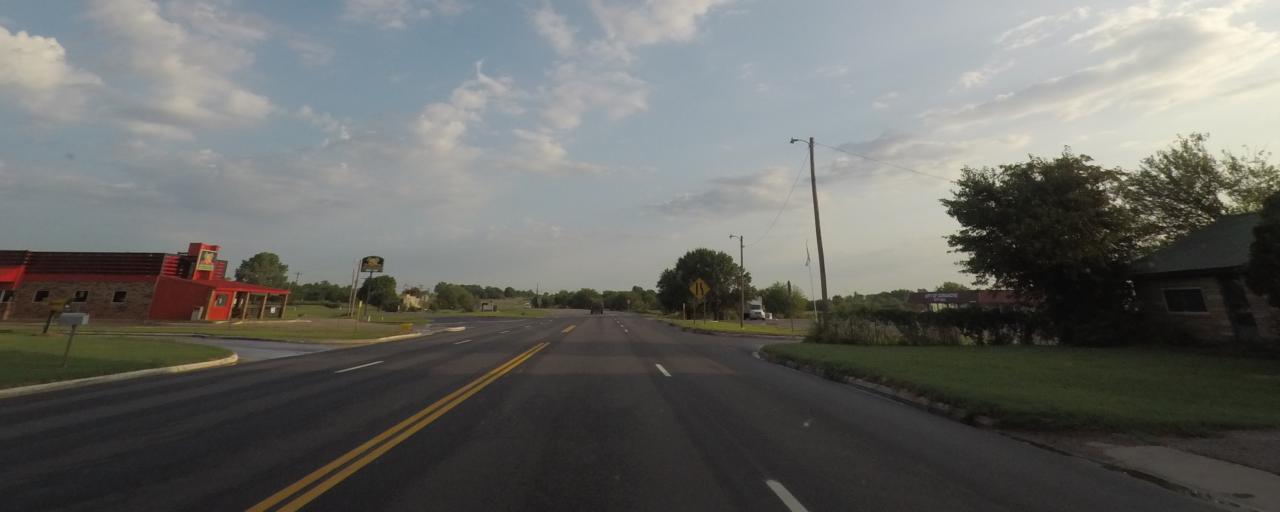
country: US
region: Oklahoma
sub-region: Stephens County
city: Comanche
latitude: 34.3724
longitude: -97.9642
